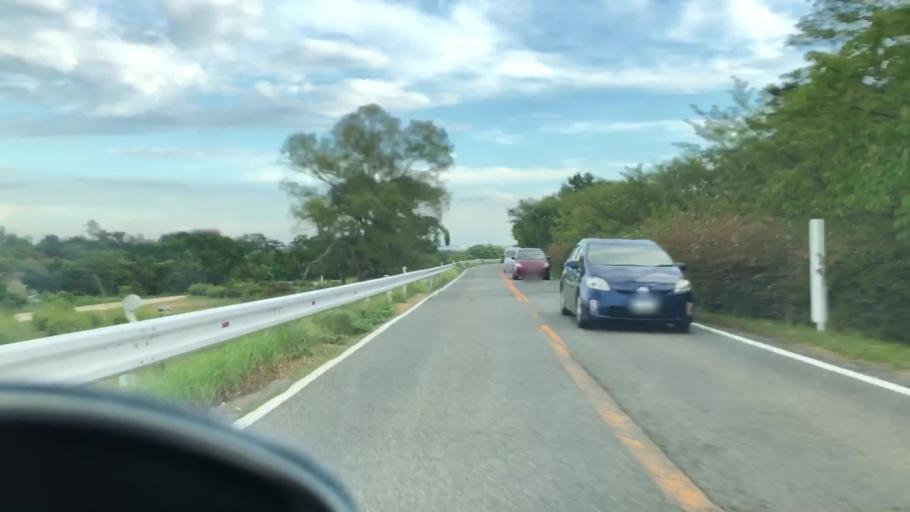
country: JP
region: Hyogo
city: Amagasaki
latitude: 34.7375
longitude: 135.3795
